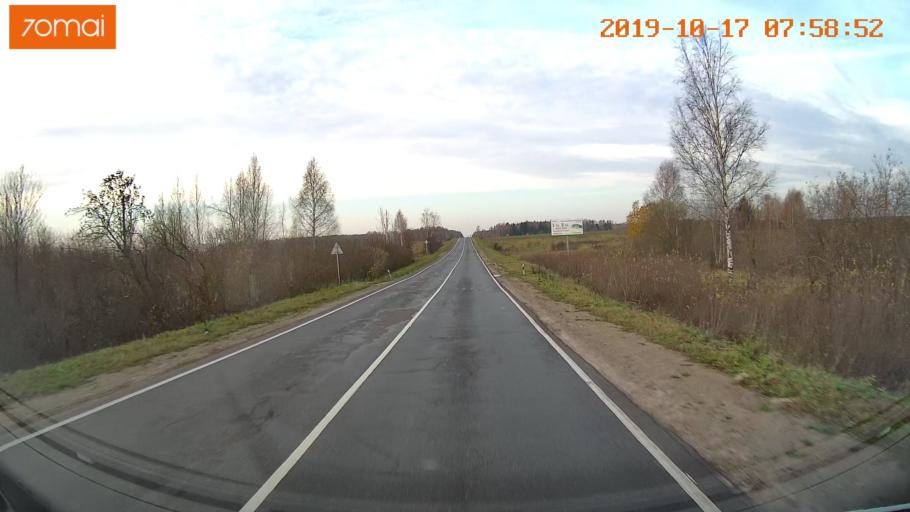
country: RU
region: Vladimir
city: Bavleny
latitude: 56.3986
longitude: 39.5495
